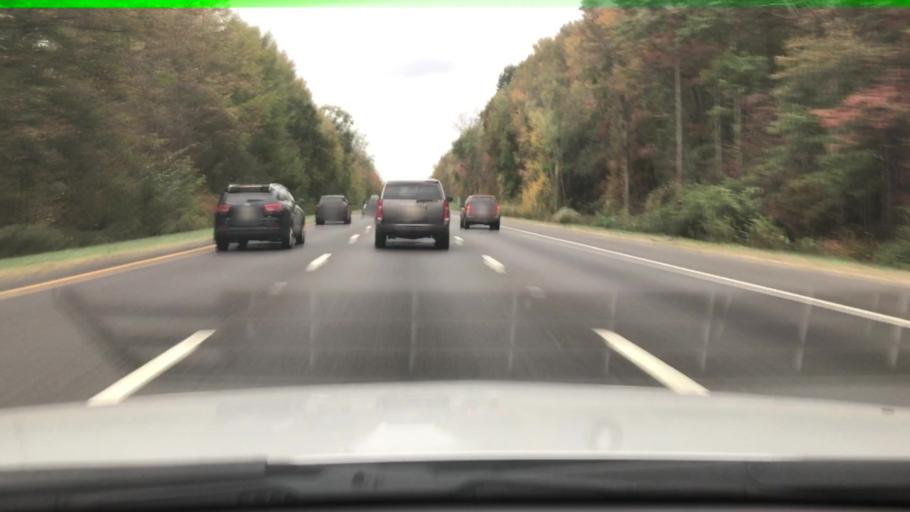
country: US
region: New Jersey
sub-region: Burlington County
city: Roebling
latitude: 40.0737
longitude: -74.7798
